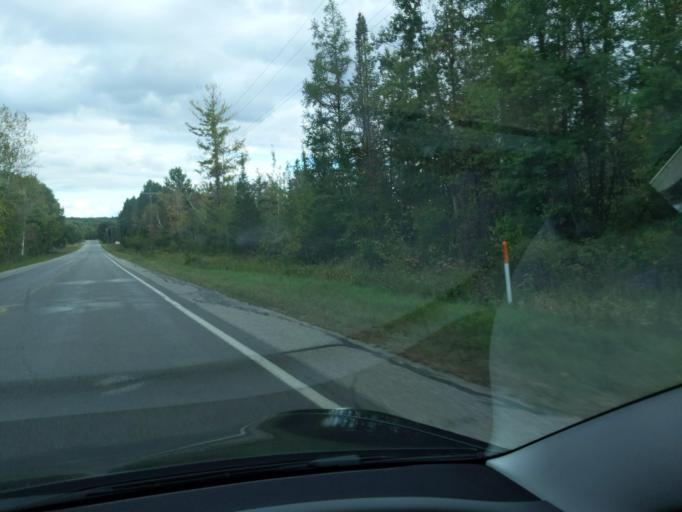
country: US
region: Michigan
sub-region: Kalkaska County
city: Rapid City
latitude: 44.8088
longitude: -85.2814
